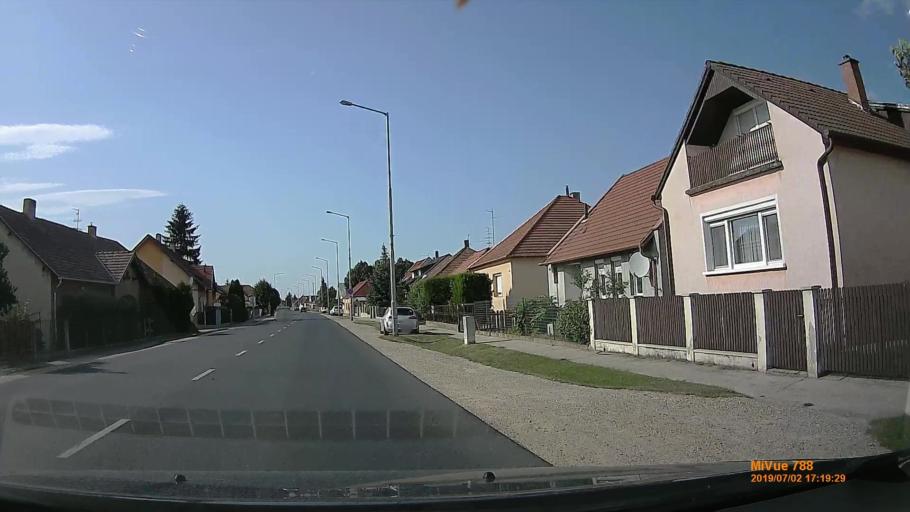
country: HU
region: Gyor-Moson-Sopron
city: Mosonmagyarovar
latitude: 47.8836
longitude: 17.2720
